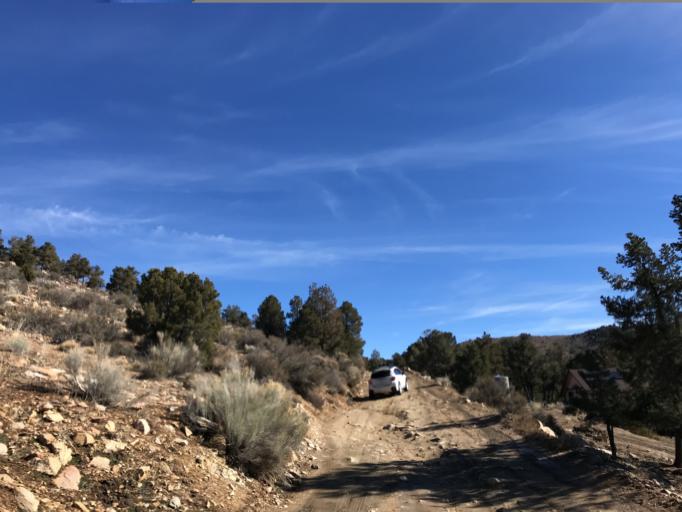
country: US
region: California
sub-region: San Bernardino County
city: Big Bear City
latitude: 34.2796
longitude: -116.7930
